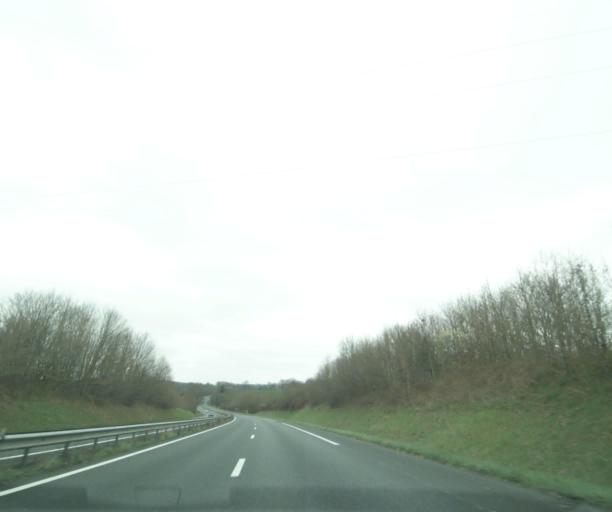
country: FR
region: Centre
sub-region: Departement de l'Indre
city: Chantome
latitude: 46.4669
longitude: 1.4963
